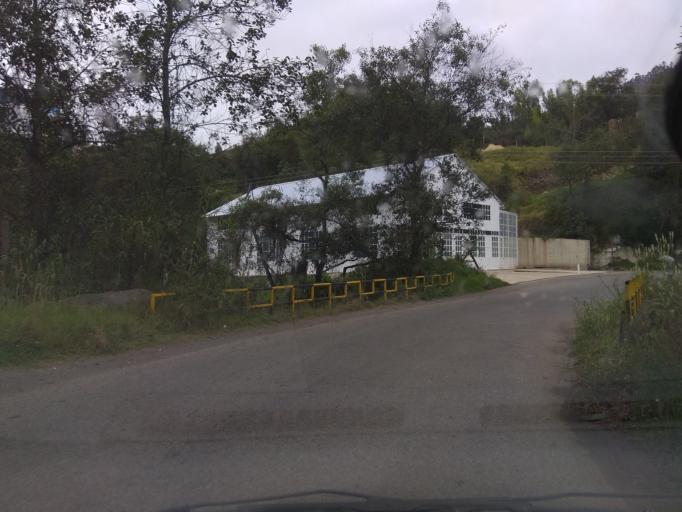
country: CO
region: Boyaca
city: Topaga
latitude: 5.7532
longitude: -72.8519
